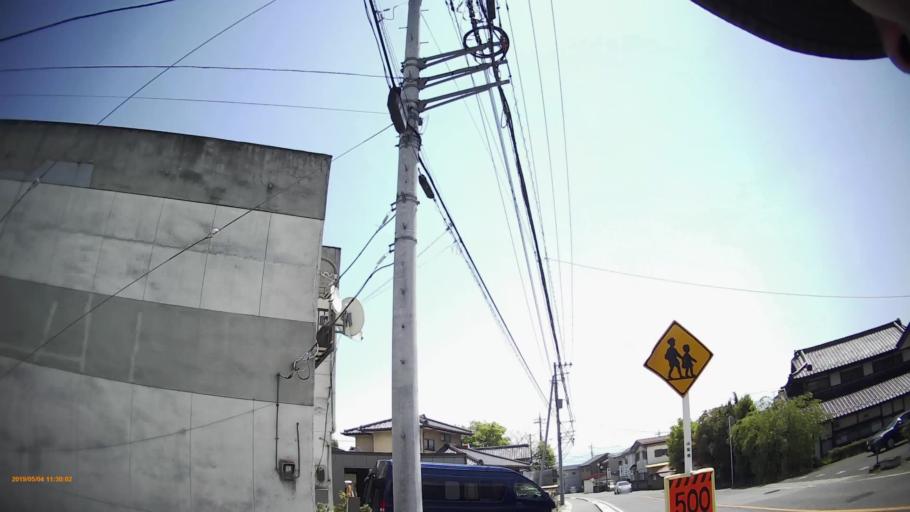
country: JP
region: Yamanashi
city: Nirasaki
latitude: 35.6905
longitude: 138.4799
